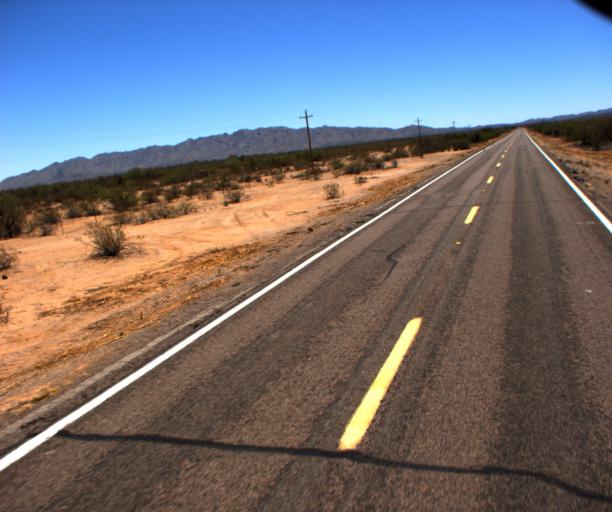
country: US
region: Arizona
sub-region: Pima County
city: Sells
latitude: 32.1820
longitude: -112.3369
